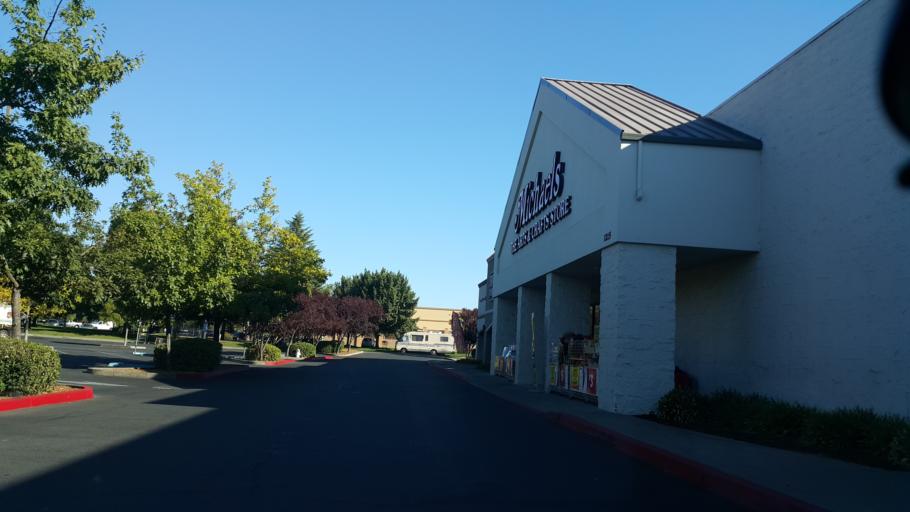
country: US
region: California
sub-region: Mendocino County
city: Ukiah
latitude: 39.1318
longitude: -123.1972
